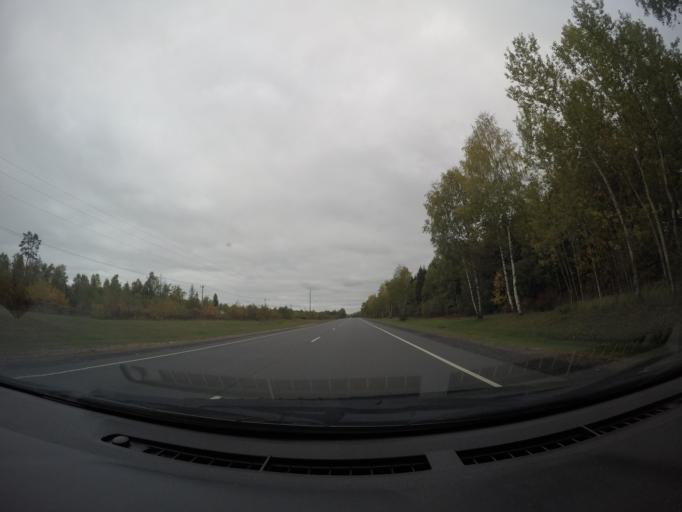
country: RU
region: Moskovskaya
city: Ruza
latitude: 55.7461
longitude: 36.2425
